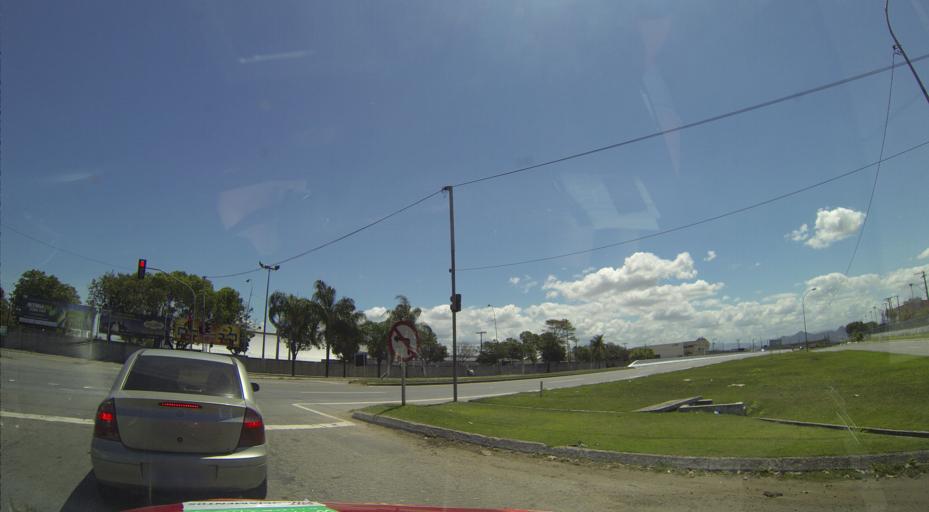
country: BR
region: Espirito Santo
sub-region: Vila Velha
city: Vila Velha
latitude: -20.2298
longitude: -40.2810
